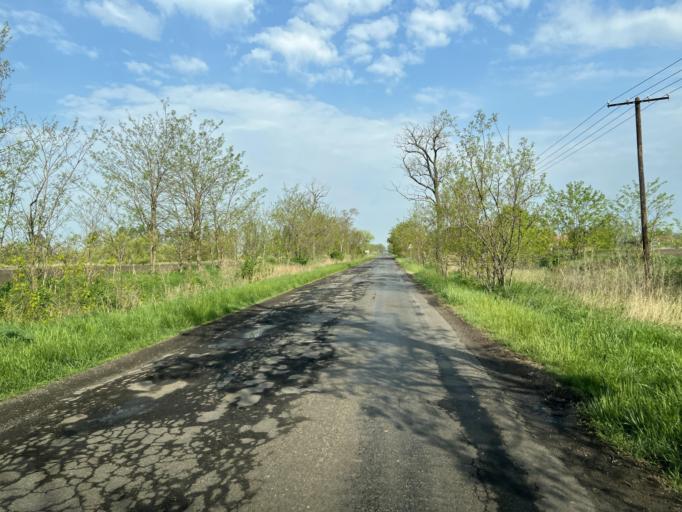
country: HU
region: Pest
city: Abony
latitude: 47.1664
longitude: 20.0364
